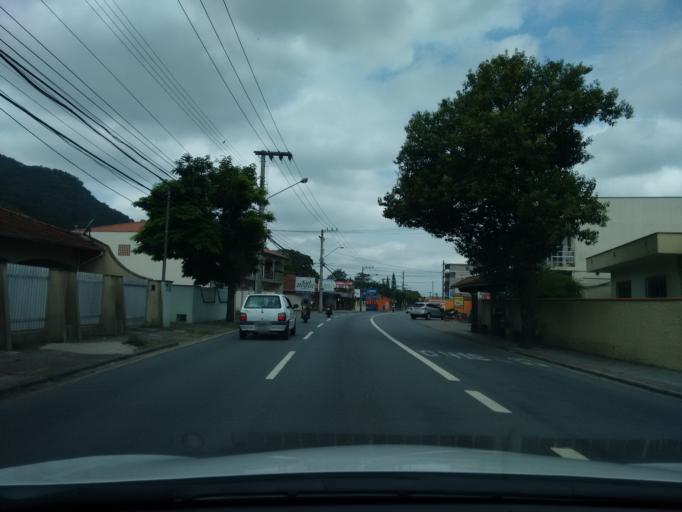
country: BR
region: Santa Catarina
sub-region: Jaragua Do Sul
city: Jaragua do Sul
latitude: -26.4801
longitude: -49.0590
